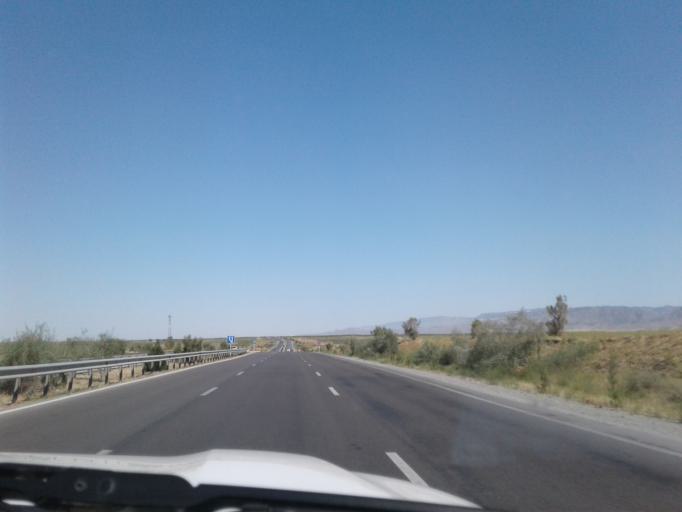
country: TM
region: Ahal
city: Annau
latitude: 37.8820
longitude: 58.6317
